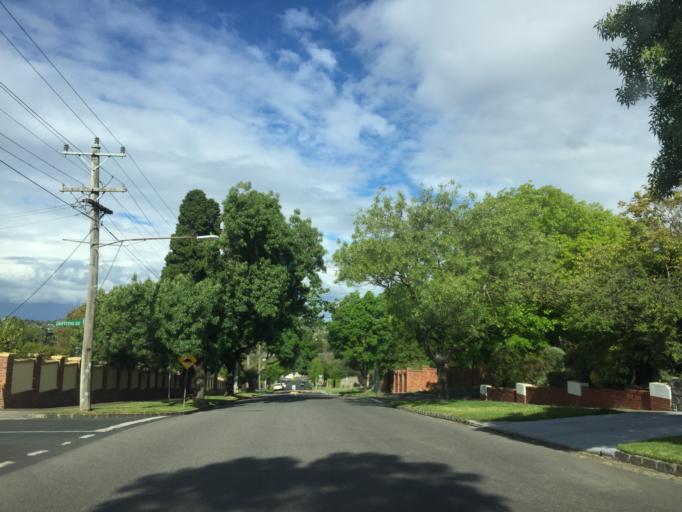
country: AU
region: Victoria
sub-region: Boroondara
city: Kew East
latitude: -37.8042
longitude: 145.0585
